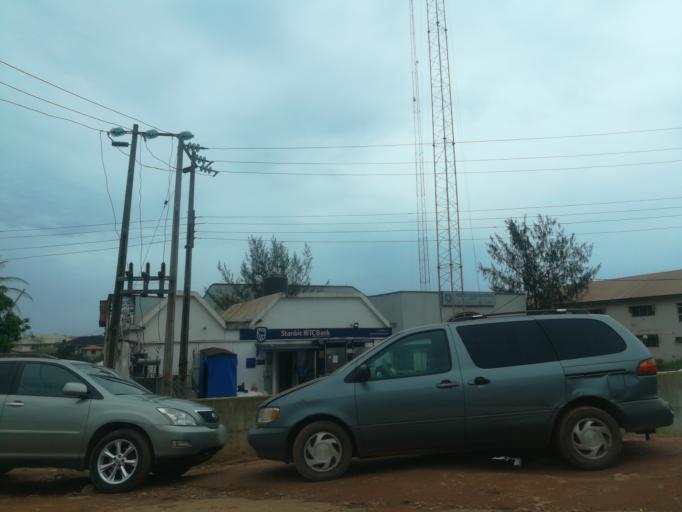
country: NG
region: Oyo
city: Ibadan
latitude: 7.3909
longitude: 3.9530
